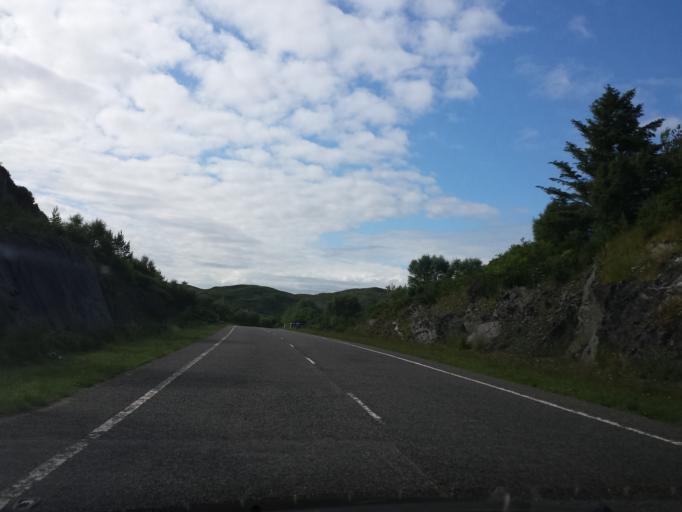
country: GB
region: Scotland
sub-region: Argyll and Bute
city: Isle Of Mull
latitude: 56.9658
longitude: -5.8218
